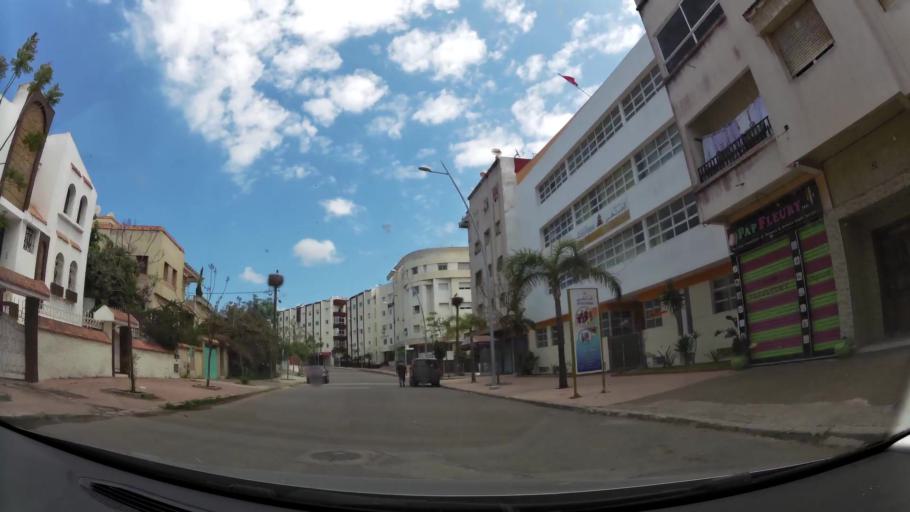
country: MA
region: Gharb-Chrarda-Beni Hssen
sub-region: Kenitra Province
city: Kenitra
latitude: 34.2657
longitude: -6.5929
